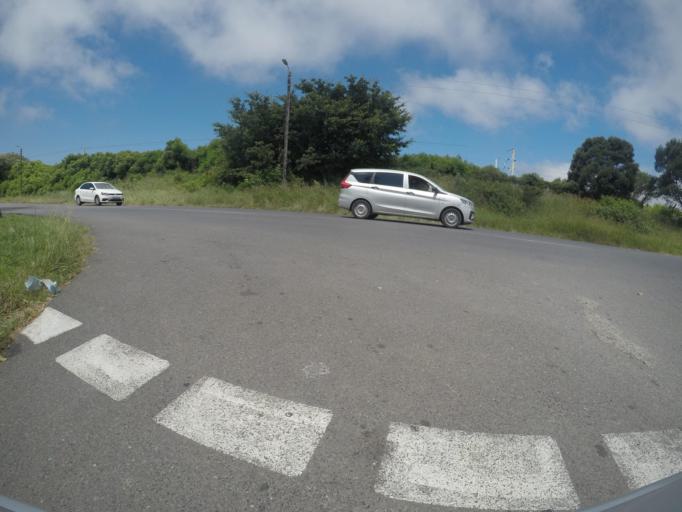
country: ZA
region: Eastern Cape
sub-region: Buffalo City Metropolitan Municipality
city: East London
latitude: -32.9797
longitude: 27.8984
